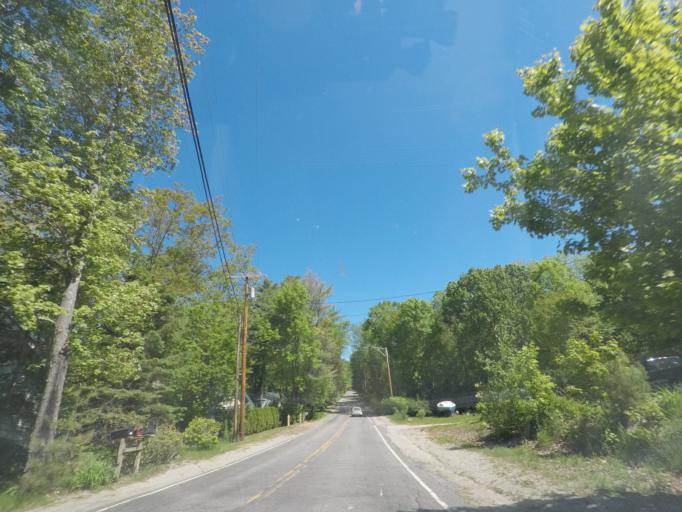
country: US
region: Maine
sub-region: Kennebec County
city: Manchester
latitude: 44.2824
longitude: -69.8894
